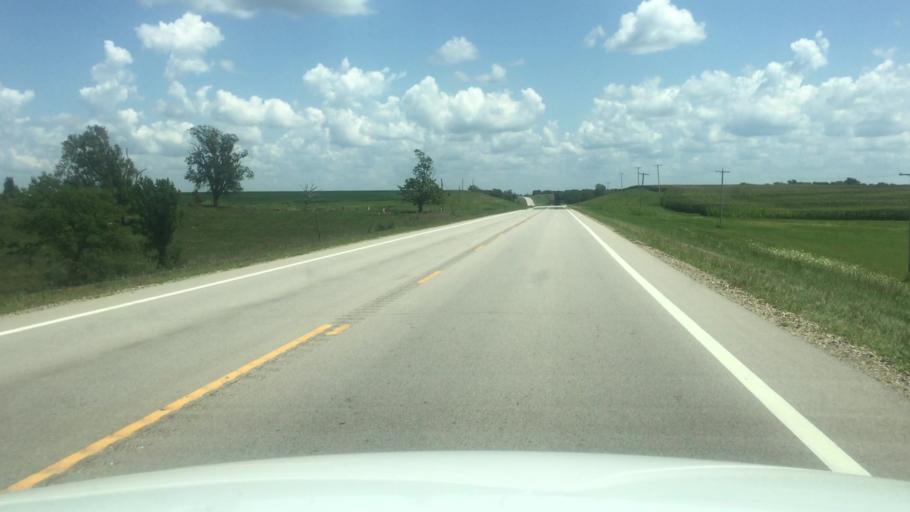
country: US
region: Kansas
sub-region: Brown County
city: Horton
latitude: 39.6676
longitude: -95.4863
